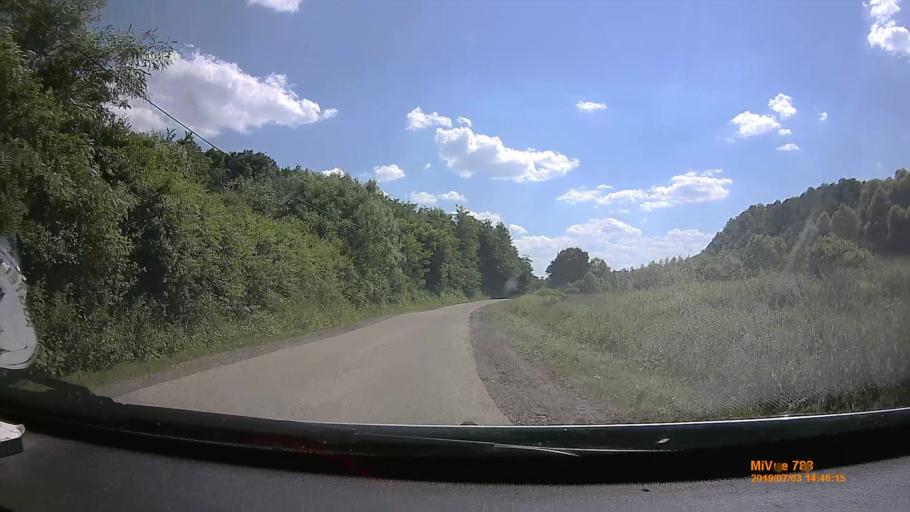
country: HU
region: Borsod-Abauj-Zemplen
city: Putnok
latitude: 48.2563
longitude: 20.4195
